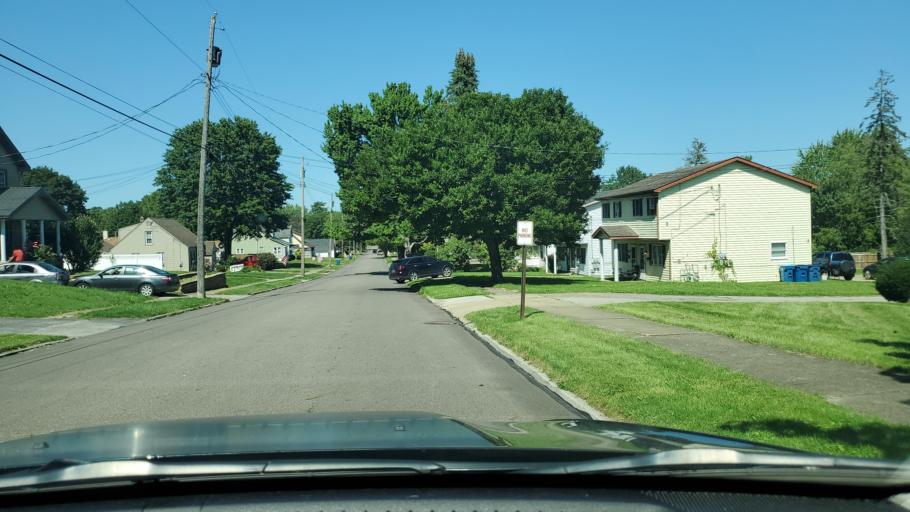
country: US
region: Ohio
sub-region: Mahoning County
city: Struthers
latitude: 41.0563
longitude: -80.6076
